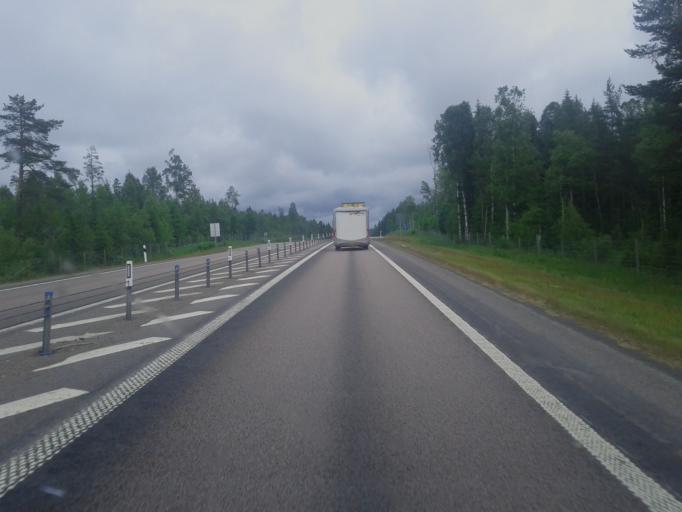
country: SE
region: Vaesternorrland
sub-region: Haernoesands Kommun
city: Haernoesand
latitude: 62.5677
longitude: 17.7363
